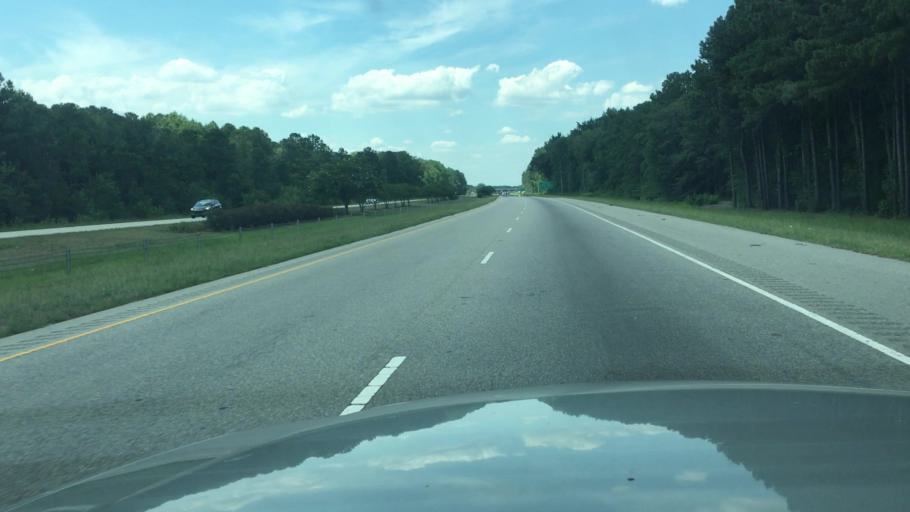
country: US
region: North Carolina
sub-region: Cumberland County
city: Fayetteville
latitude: 34.9969
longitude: -78.8632
